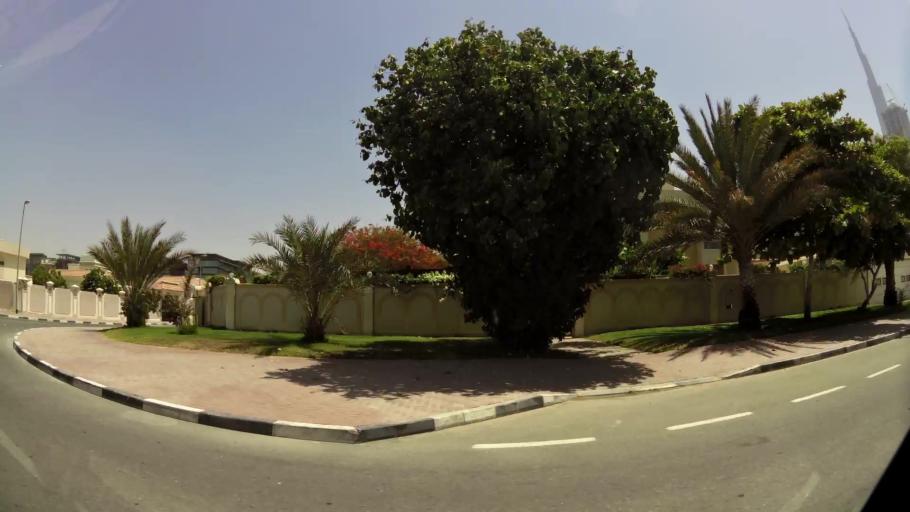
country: AE
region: Dubai
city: Dubai
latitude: 25.1990
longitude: 55.2615
